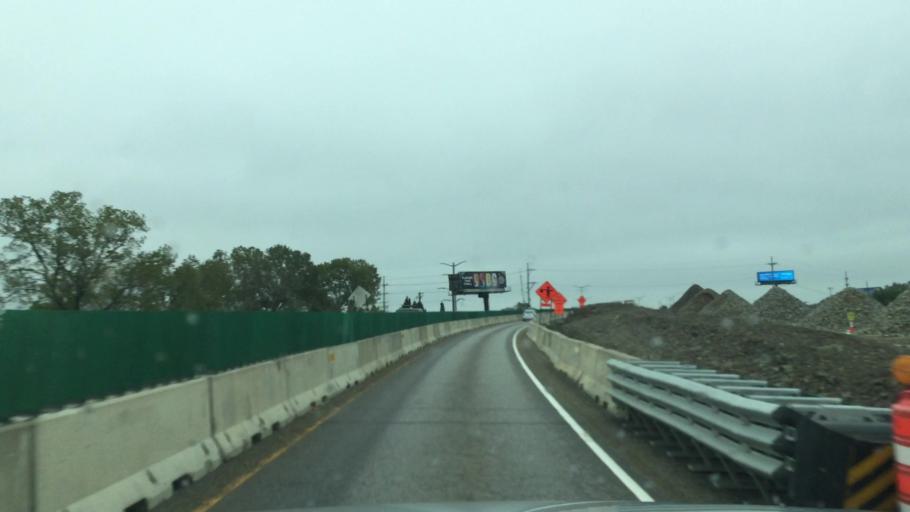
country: US
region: Illinois
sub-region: Lake County
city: Deerfield
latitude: 42.1495
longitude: -87.8421
